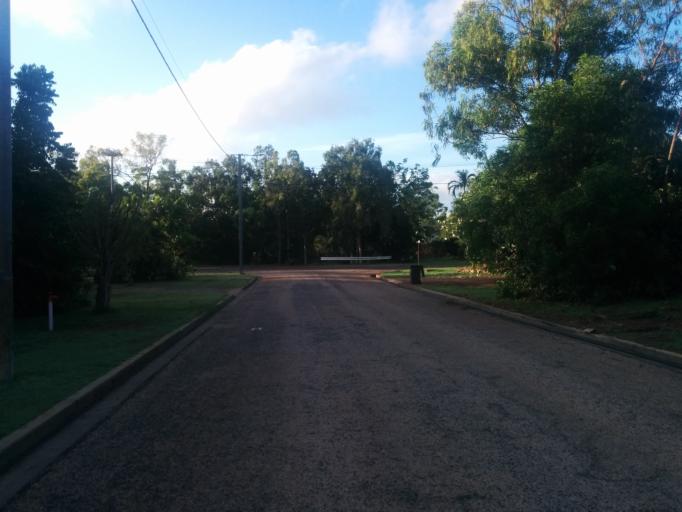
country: AU
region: Northern Territory
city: Alyangula
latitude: -13.8446
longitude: 136.4163
